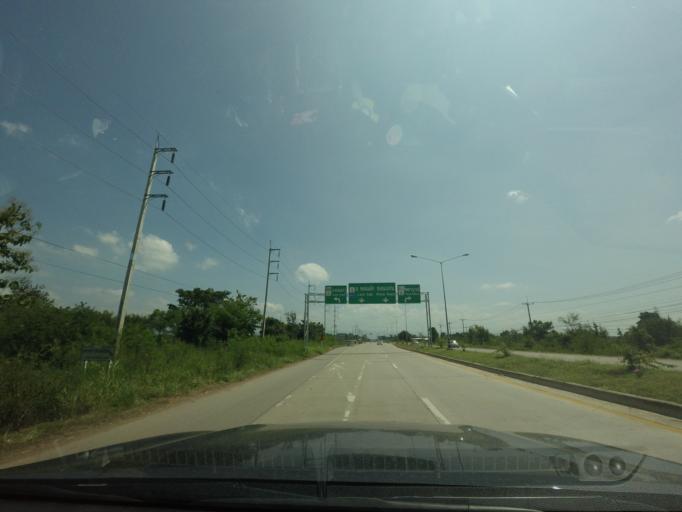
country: TH
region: Phetchabun
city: Lom Sak
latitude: 16.7664
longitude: 101.1836
